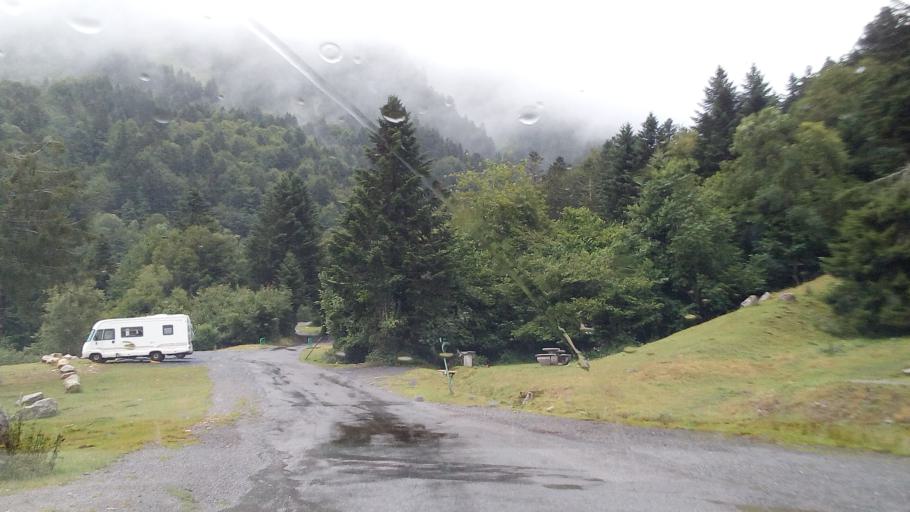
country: FR
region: Midi-Pyrenees
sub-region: Departement des Hautes-Pyrenees
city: Cauterets
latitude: 42.9112
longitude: -0.2588
